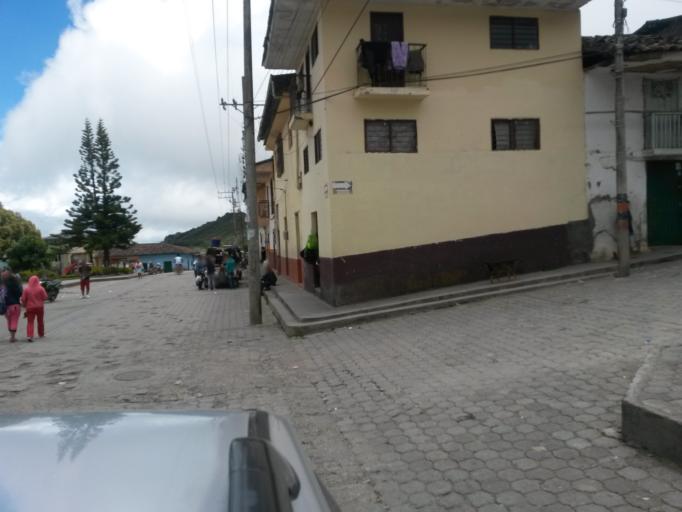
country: CO
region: Cauca
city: Almaguer
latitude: 1.9151
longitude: -76.8542
